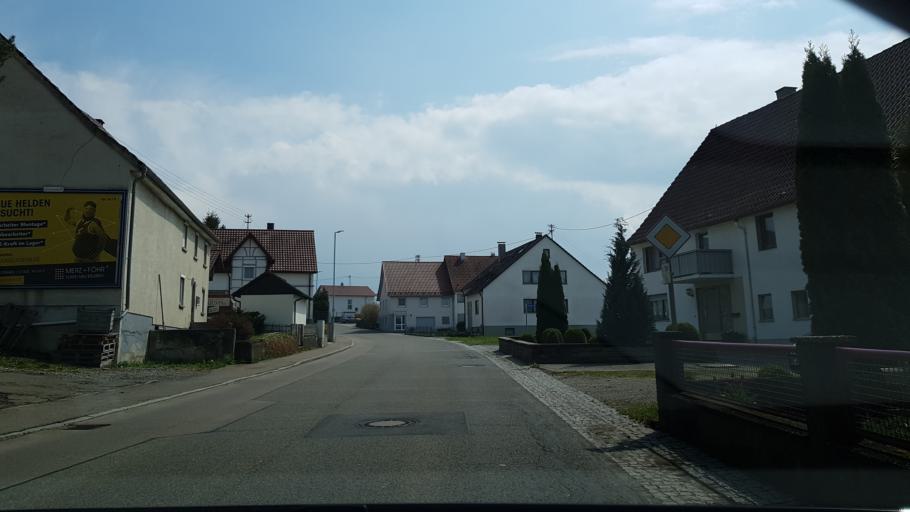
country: DE
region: Baden-Wuerttemberg
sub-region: Tuebingen Region
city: Wain
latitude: 48.2103
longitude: 10.0203
